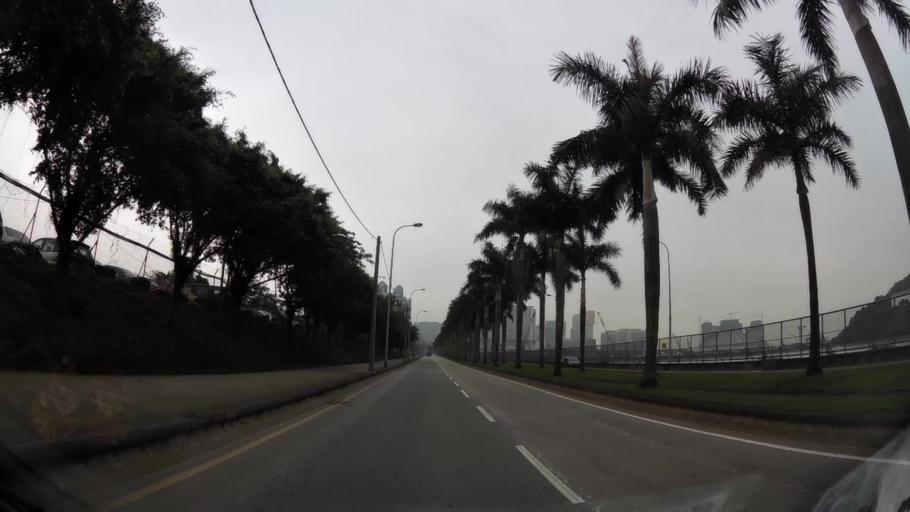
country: MO
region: Macau
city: Macau
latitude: 22.1326
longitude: 113.5629
